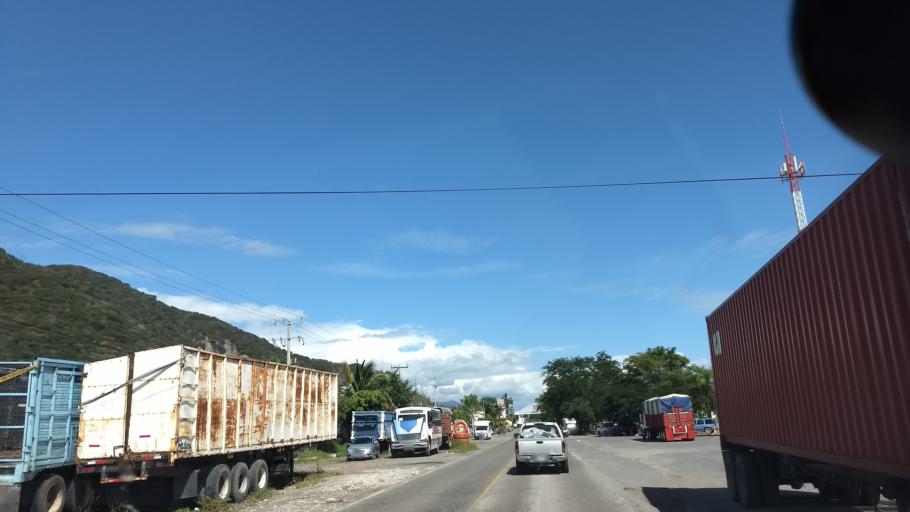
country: MX
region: Jalisco
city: Tuxpan
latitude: 19.5545
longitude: -103.3899
